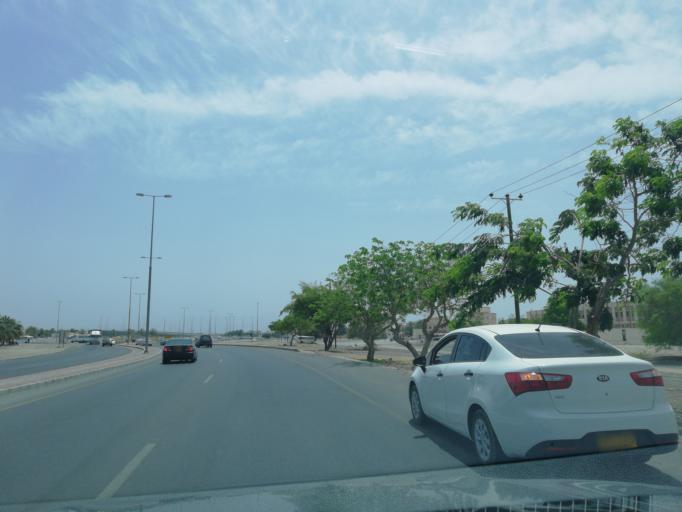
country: OM
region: Muhafazat Masqat
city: As Sib al Jadidah
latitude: 23.6716
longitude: 58.1631
